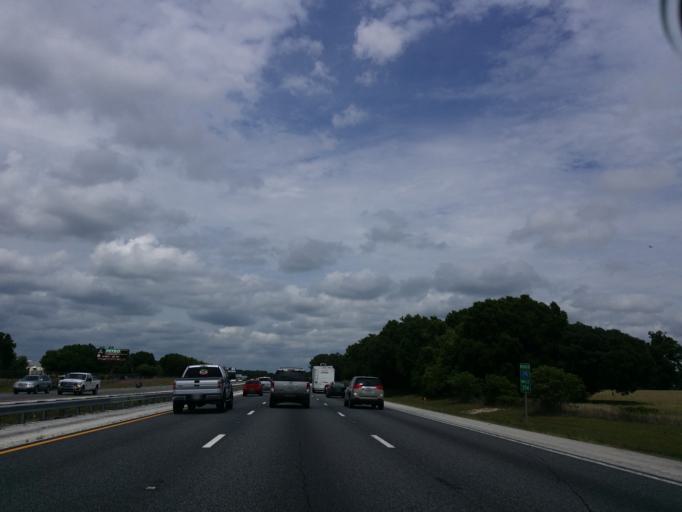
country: US
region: Florida
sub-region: Marion County
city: Ocala
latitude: 29.2422
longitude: -82.1898
